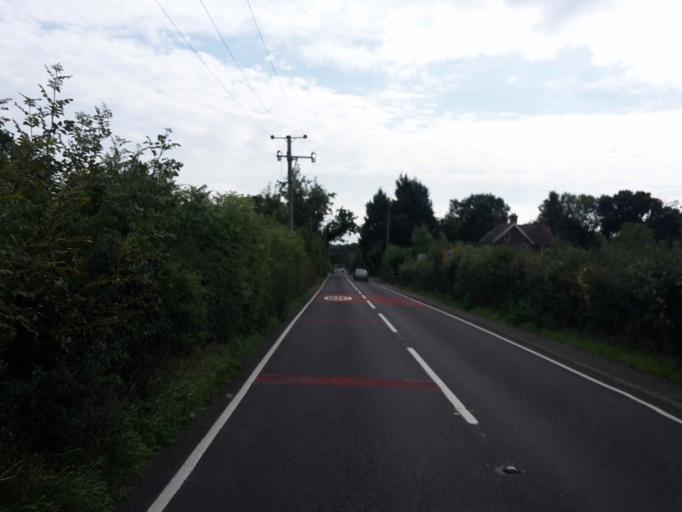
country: GB
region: England
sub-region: West Sussex
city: Billingshurst
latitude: 50.9951
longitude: -0.4103
